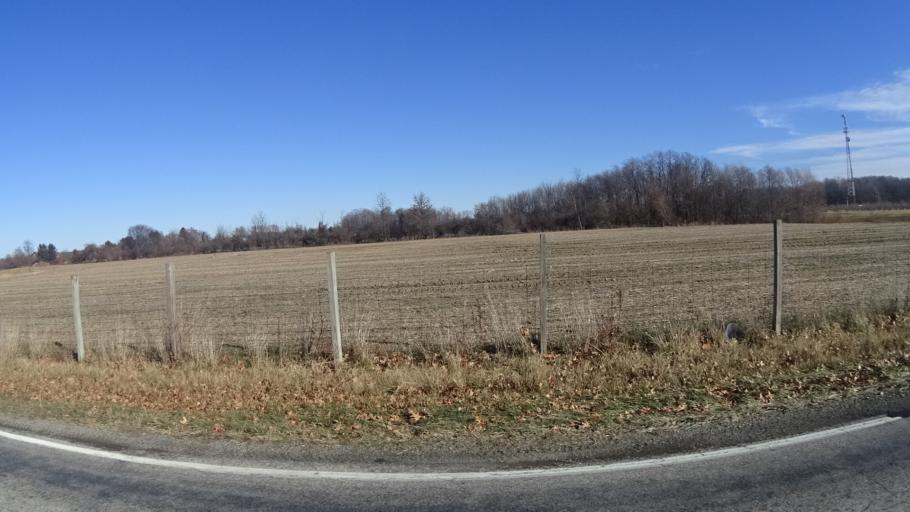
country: US
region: Ohio
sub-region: Lorain County
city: South Amherst
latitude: 41.3645
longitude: -82.3021
